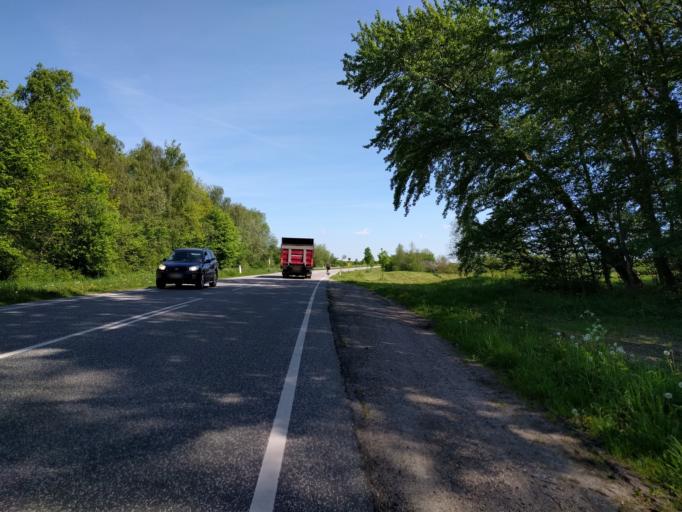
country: DK
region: Zealand
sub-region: Guldborgsund Kommune
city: Nykobing Falster
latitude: 54.7546
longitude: 11.9062
